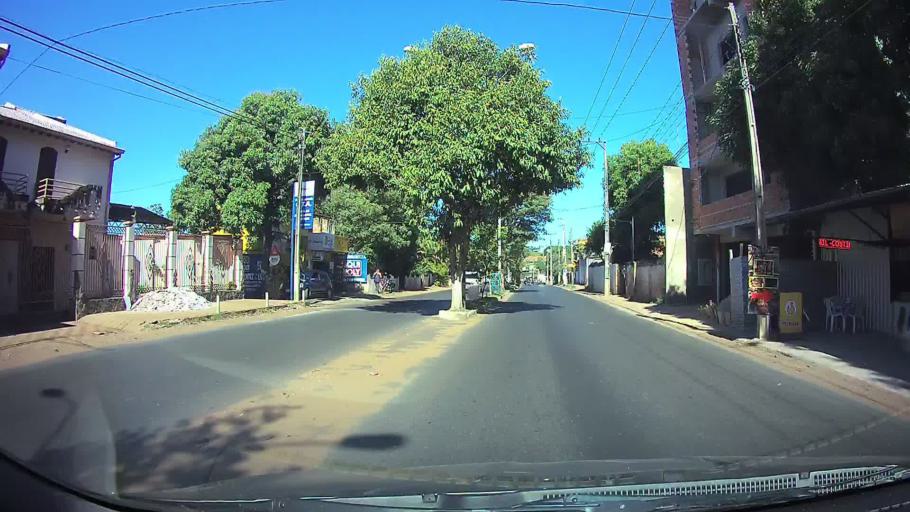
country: PY
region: Central
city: Villa Elisa
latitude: -25.3643
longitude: -57.5775
